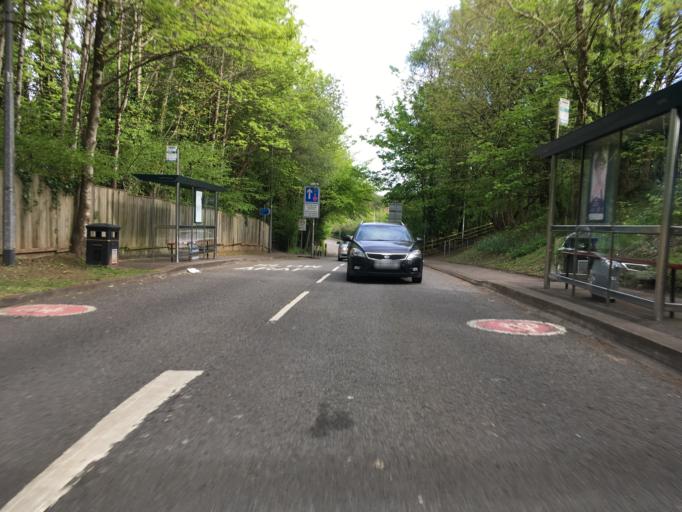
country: GB
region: Wales
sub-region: Cardiff
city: Radyr
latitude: 51.5290
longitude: -3.2449
